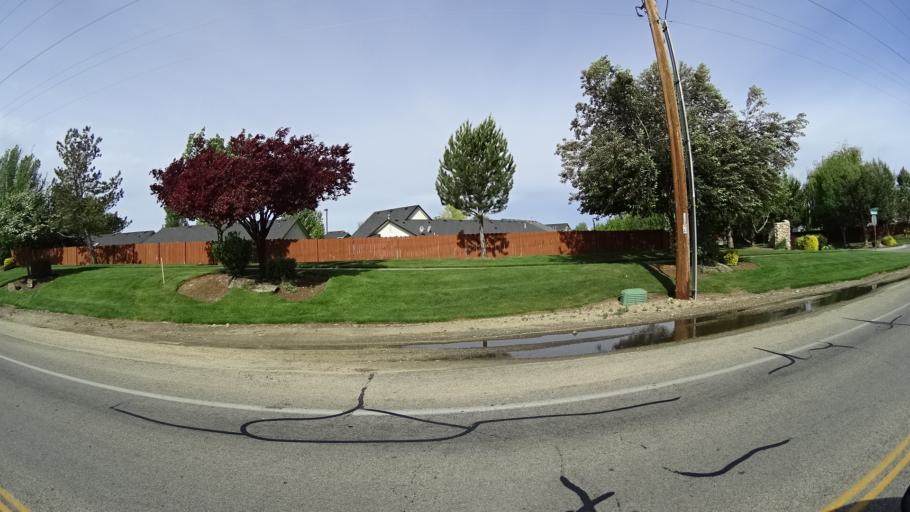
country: US
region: Idaho
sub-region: Ada County
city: Meridian
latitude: 43.5513
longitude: -116.3344
